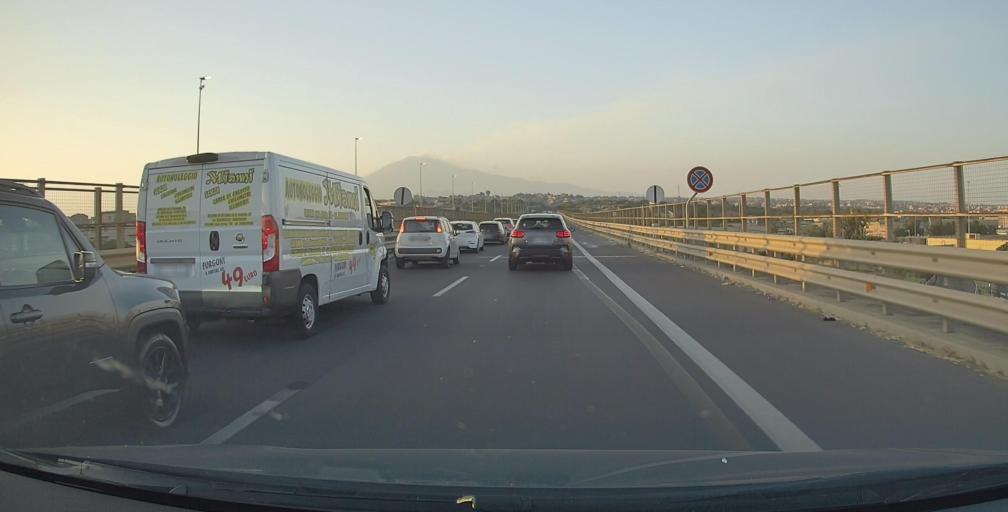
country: IT
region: Sicily
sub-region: Catania
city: Misterbianco
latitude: 37.5122
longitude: 15.0193
